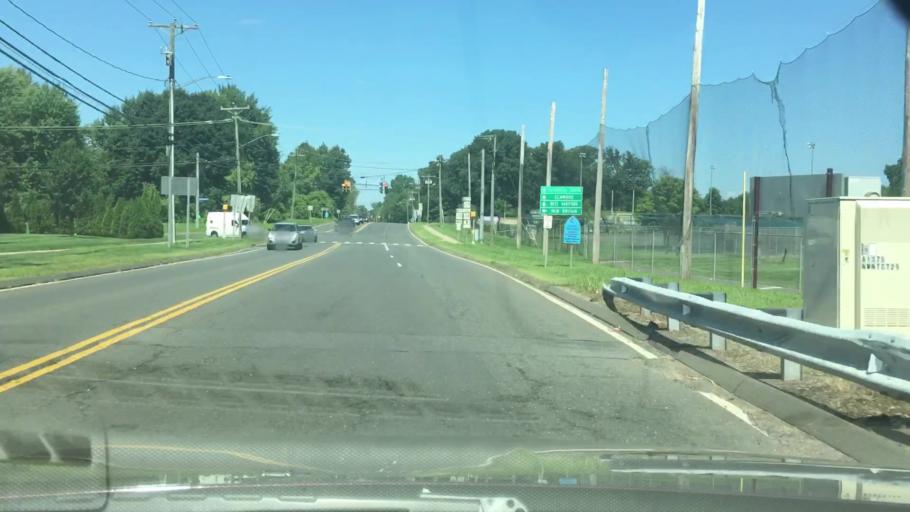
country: US
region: Connecticut
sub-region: Hartford County
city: Newington
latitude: 41.6745
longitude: -72.7290
